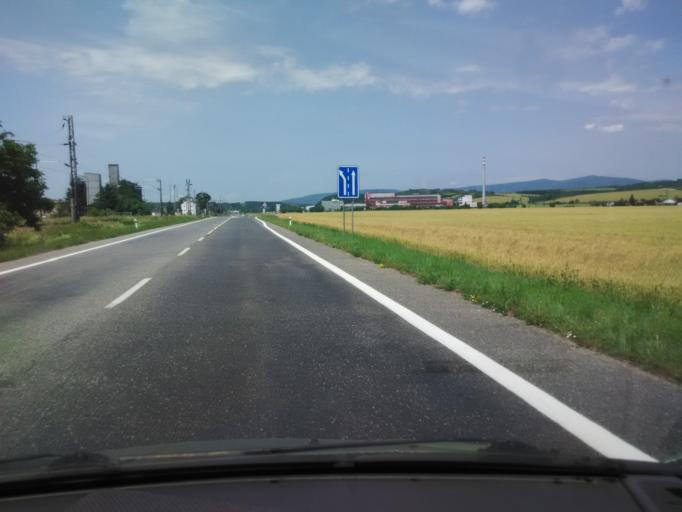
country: SK
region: Nitriansky
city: Tlmace
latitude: 48.2768
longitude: 18.5535
